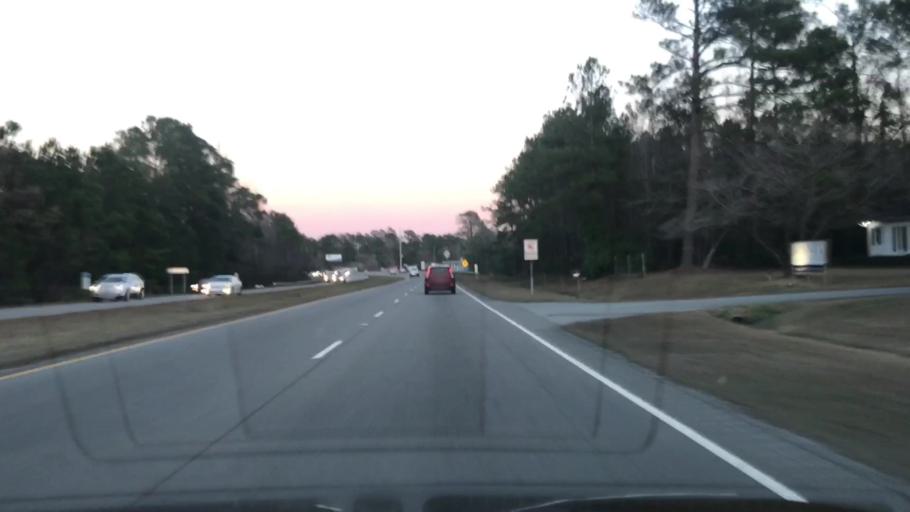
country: US
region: North Carolina
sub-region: Brunswick County
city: Shallotte
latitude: 34.0184
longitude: -78.2699
